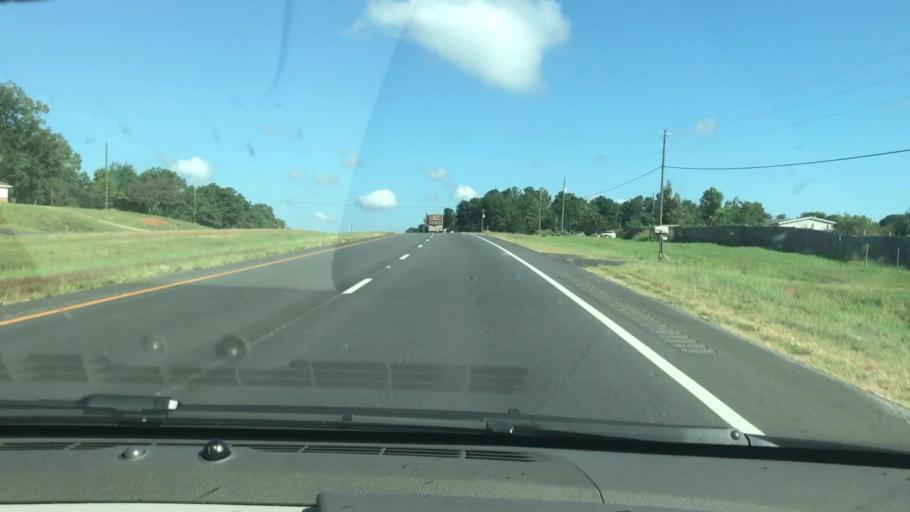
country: US
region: Alabama
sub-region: Barbour County
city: Eufaula
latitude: 32.0275
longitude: -85.1203
